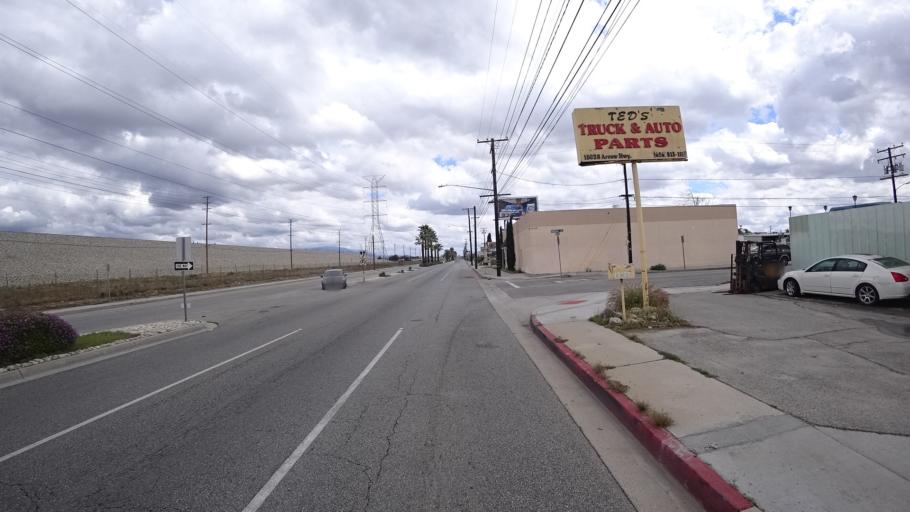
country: US
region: California
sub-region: Los Angeles County
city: Irwindale
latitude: 34.1069
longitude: -117.9510
